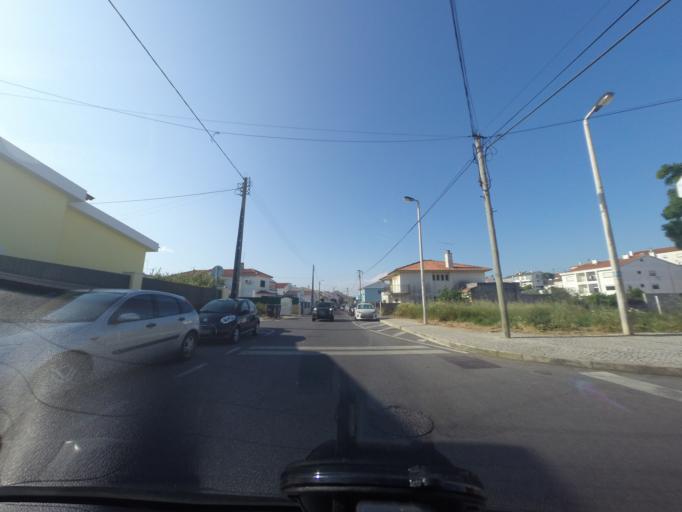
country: PT
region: Lisbon
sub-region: Cascais
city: Sao Domingos de Rana
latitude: 38.7129
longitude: -9.3445
